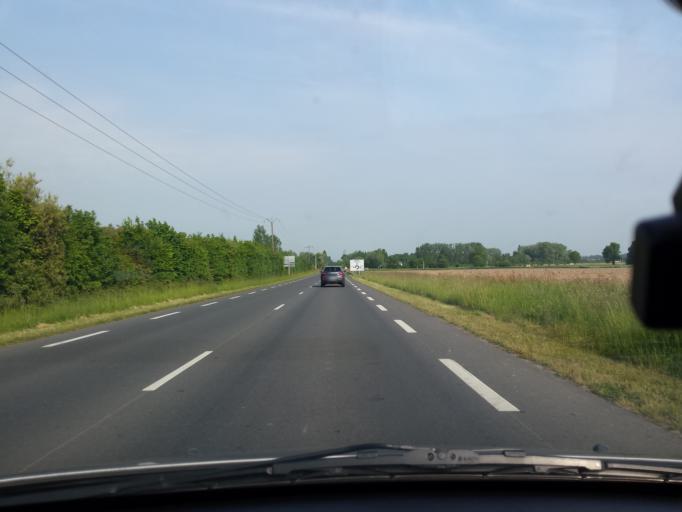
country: FR
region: Pays de la Loire
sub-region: Departement de la Loire-Atlantique
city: Machecoul
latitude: 46.9929
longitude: -1.8027
